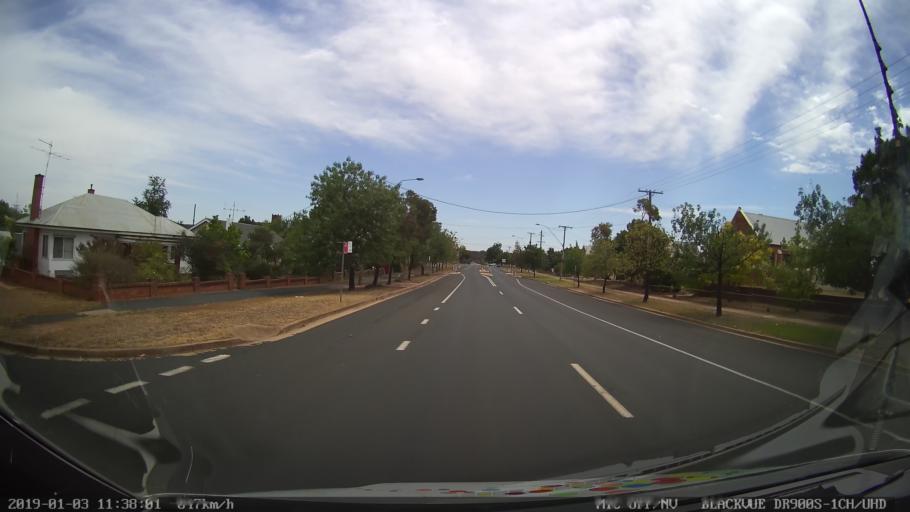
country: AU
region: New South Wales
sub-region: Weddin
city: Grenfell
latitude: -33.8989
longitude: 148.1620
